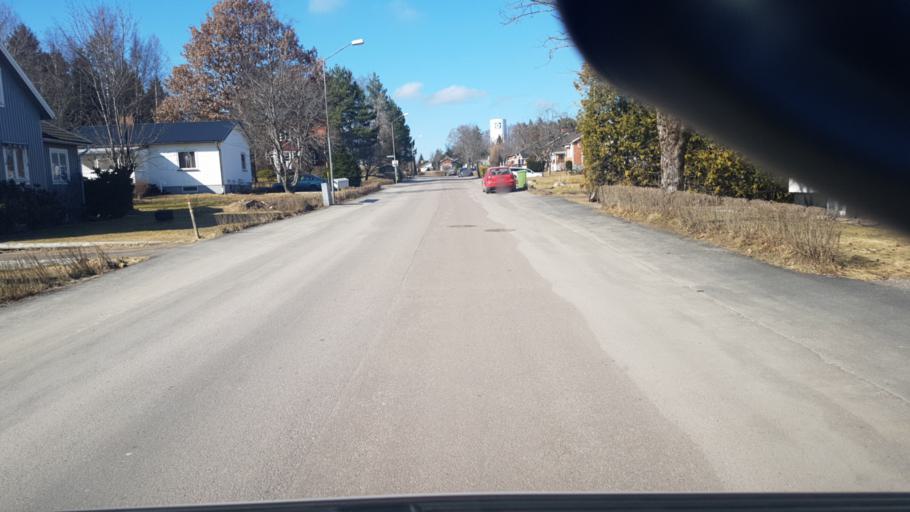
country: SE
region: Vaermland
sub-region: Eda Kommun
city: Charlottenberg
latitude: 59.8854
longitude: 12.3069
